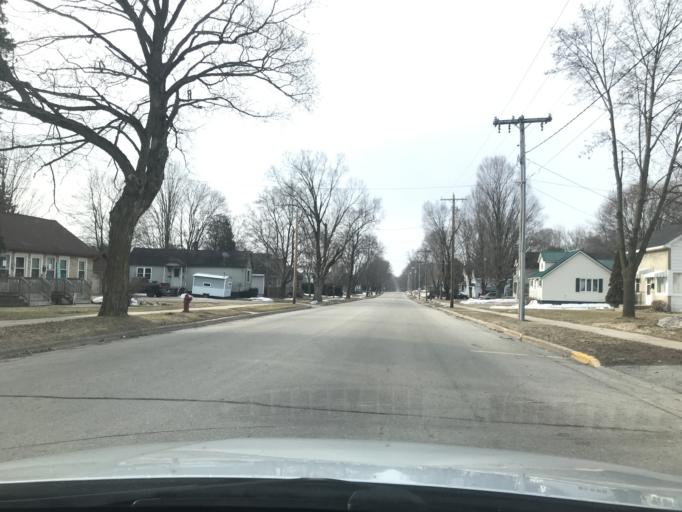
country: US
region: Wisconsin
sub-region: Oconto County
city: Oconto Falls
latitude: 44.8712
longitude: -88.1466
